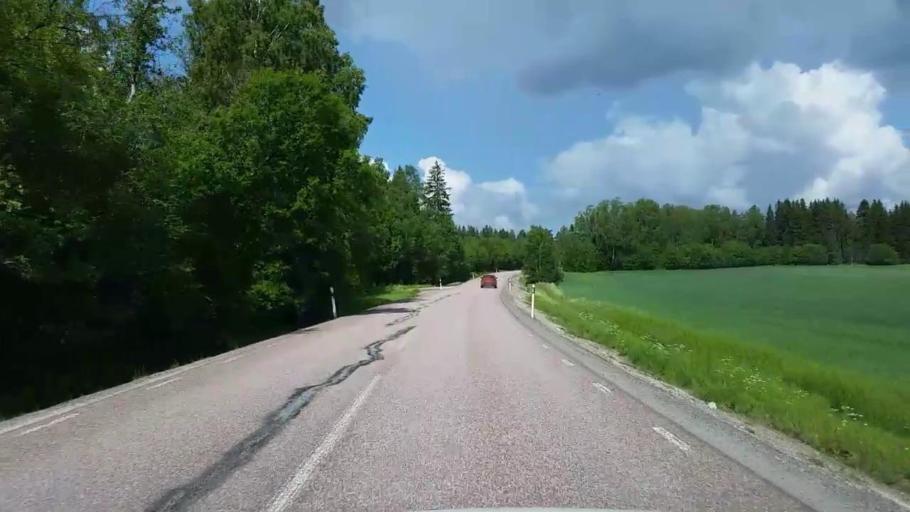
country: SE
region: Vaestmanland
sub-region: Skinnskattebergs Kommun
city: Skinnskatteberg
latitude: 59.7923
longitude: 15.8528
